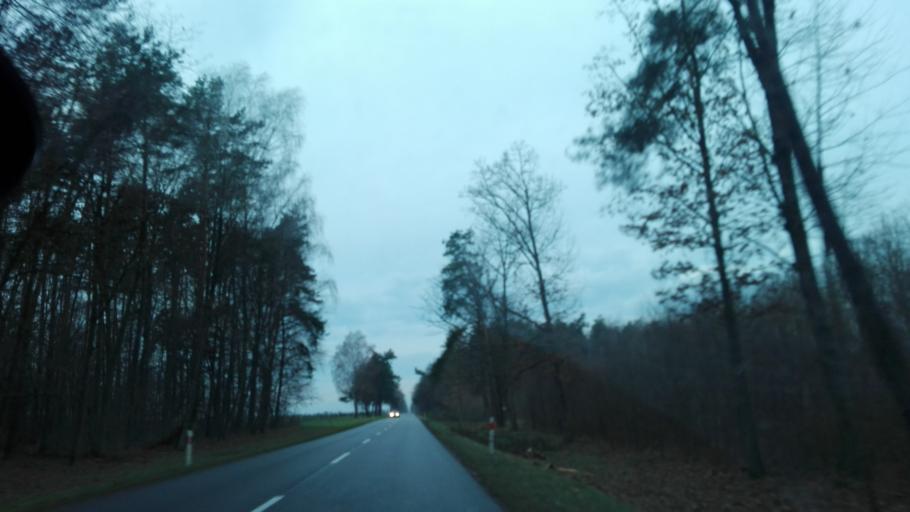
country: PL
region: Lublin Voivodeship
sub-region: Powiat radzynski
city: Wohyn
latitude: 51.7782
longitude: 22.8327
